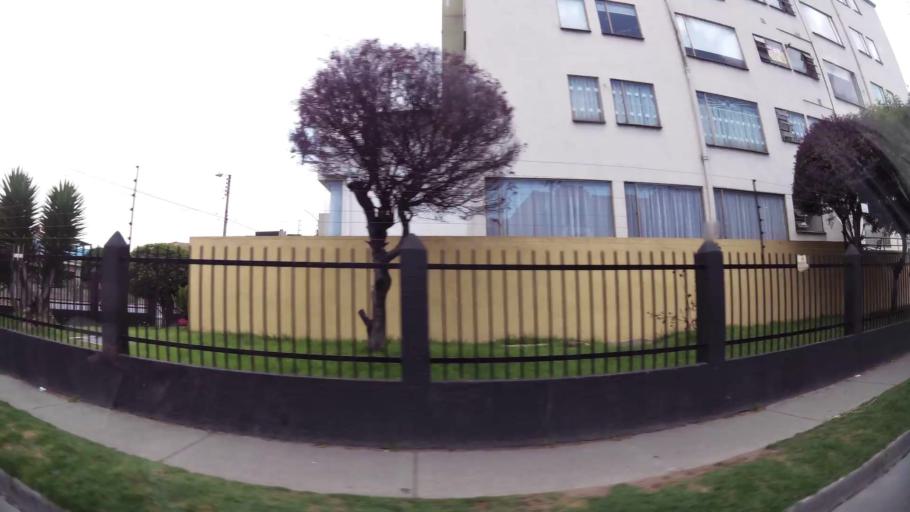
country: CO
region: Cundinamarca
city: La Calera
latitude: 4.7434
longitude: -74.0298
